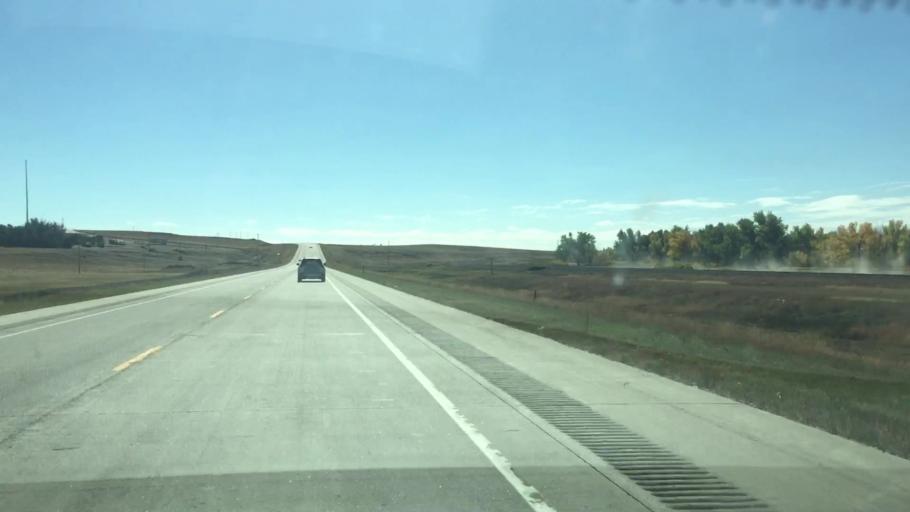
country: US
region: Colorado
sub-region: Lincoln County
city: Limon
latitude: 39.2190
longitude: -103.6053
